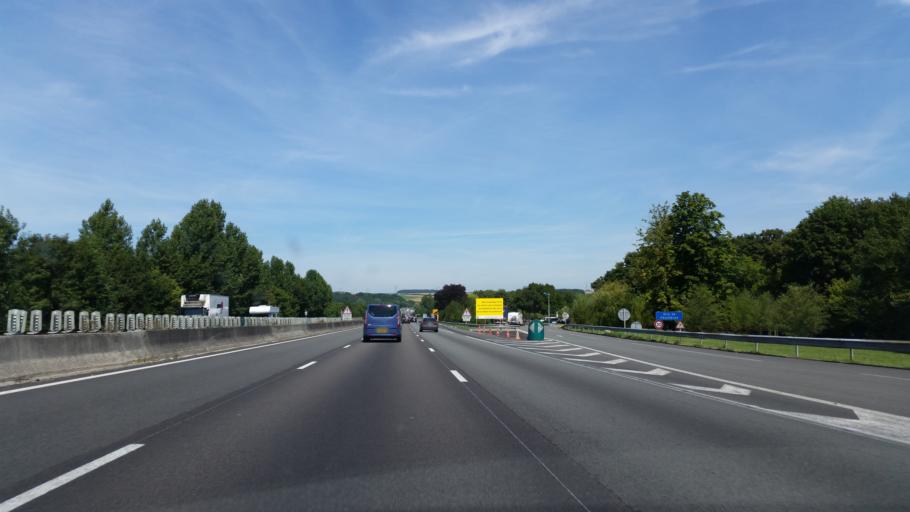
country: FR
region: Picardie
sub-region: Departement de la Somme
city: Peronne
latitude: 49.9430
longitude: 2.8524
